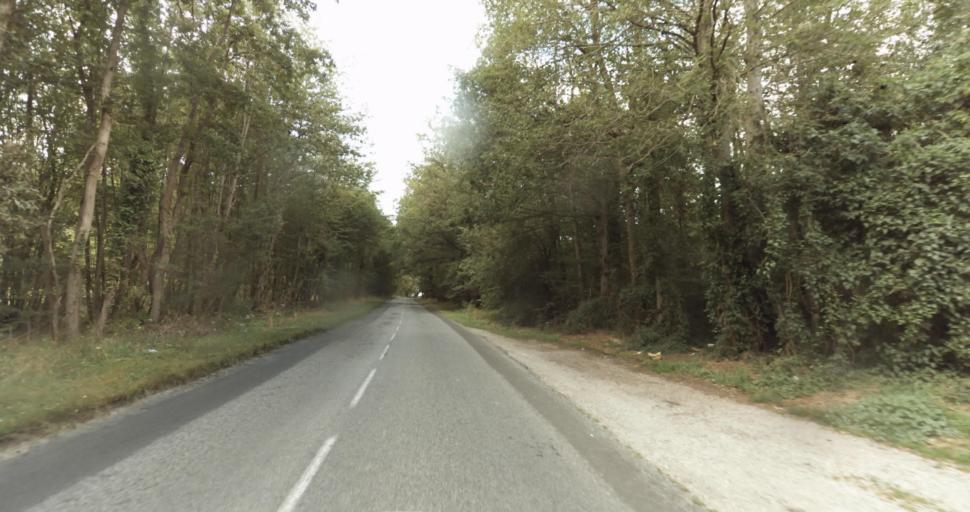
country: FR
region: Haute-Normandie
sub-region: Departement de l'Eure
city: La Couture-Boussey
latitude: 48.8827
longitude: 1.4089
